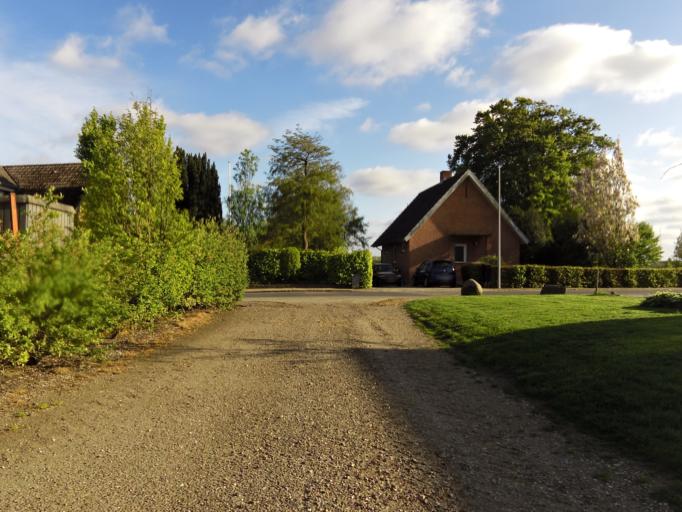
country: DK
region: South Denmark
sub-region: Vejen Kommune
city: Rodding
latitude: 55.3307
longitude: 9.0553
